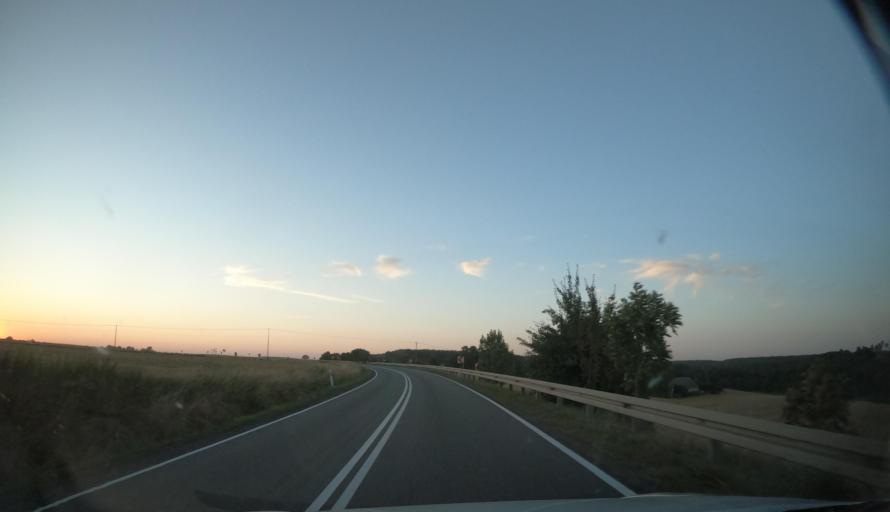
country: PL
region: Kujawsko-Pomorskie
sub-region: Powiat bydgoski
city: Koronowo
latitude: 53.3670
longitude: 17.8636
